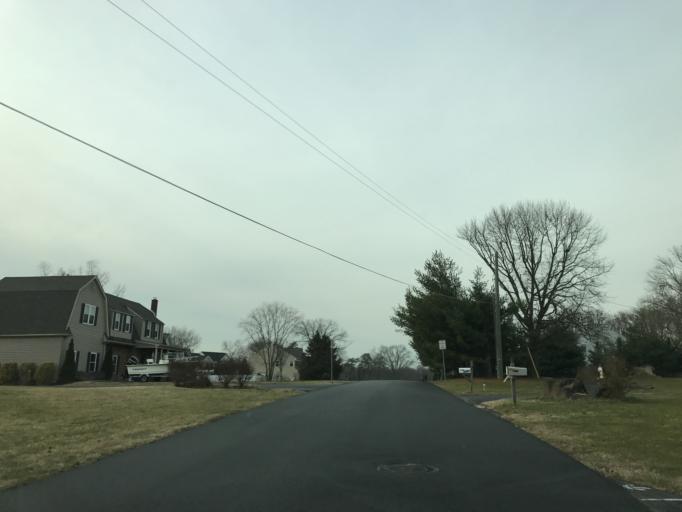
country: US
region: Maryland
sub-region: Baltimore County
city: White Marsh
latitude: 39.4082
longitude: -76.4069
